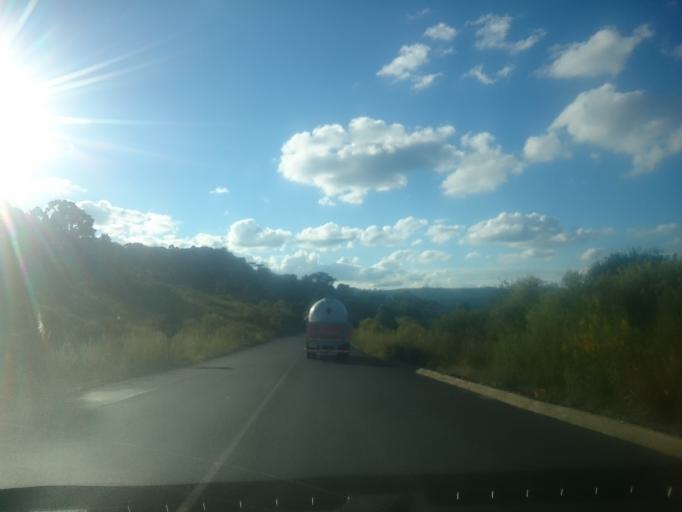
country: BR
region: Santa Catarina
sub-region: Sao Joaquim
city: Sao Joaquim
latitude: -28.0988
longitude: -50.0519
